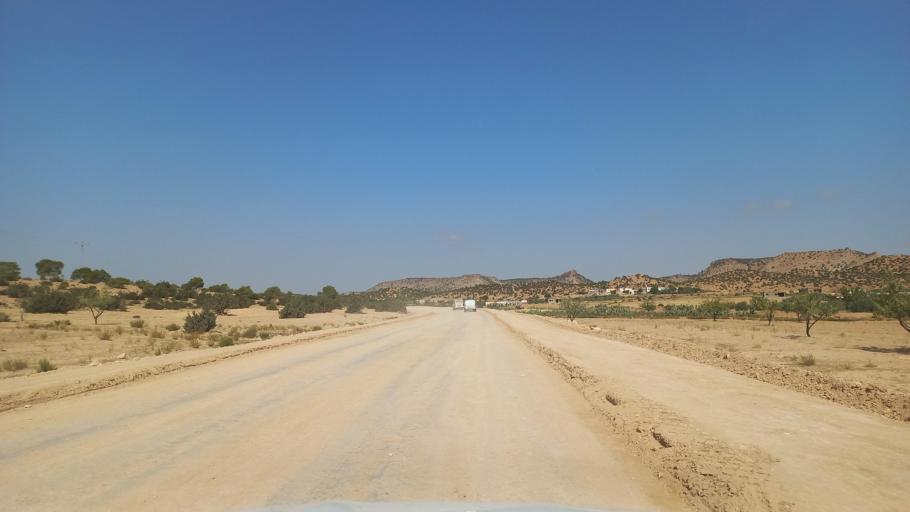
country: TN
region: Al Qasrayn
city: Sbiba
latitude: 35.4034
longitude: 8.9965
